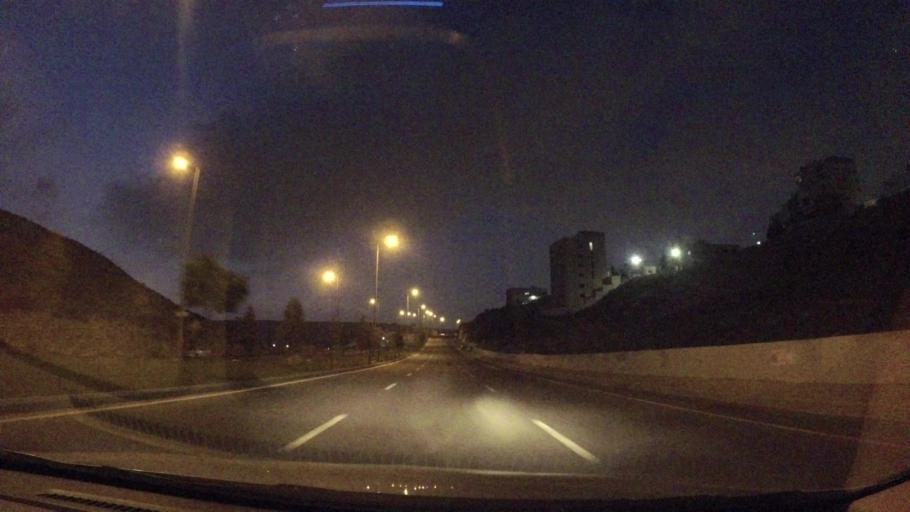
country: JO
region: Amman
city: Al Bunayyat ash Shamaliyah
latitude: 31.9211
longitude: 35.8794
